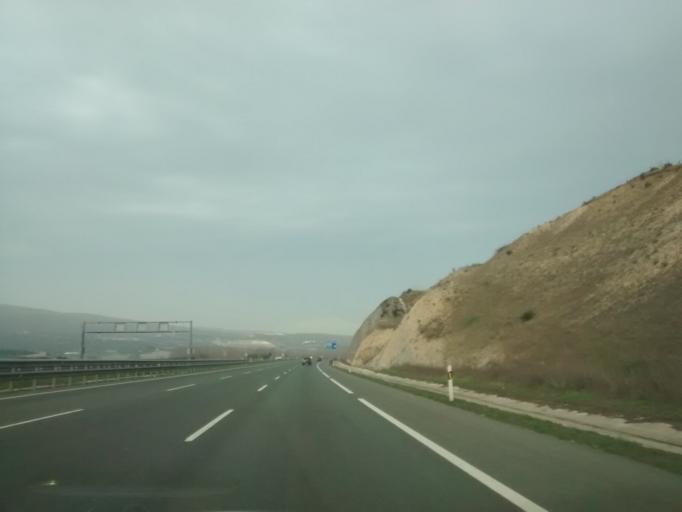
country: ES
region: Basque Country
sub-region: Provincia de Alava
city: Arminon
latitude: 42.7930
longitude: -2.8213
